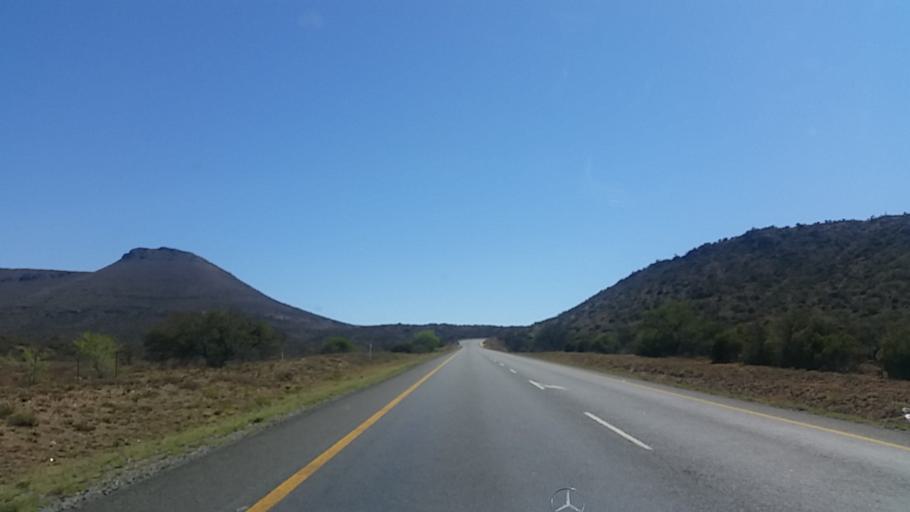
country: ZA
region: Eastern Cape
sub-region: Cacadu District Municipality
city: Graaff-Reinet
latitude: -32.0672
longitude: 24.6061
